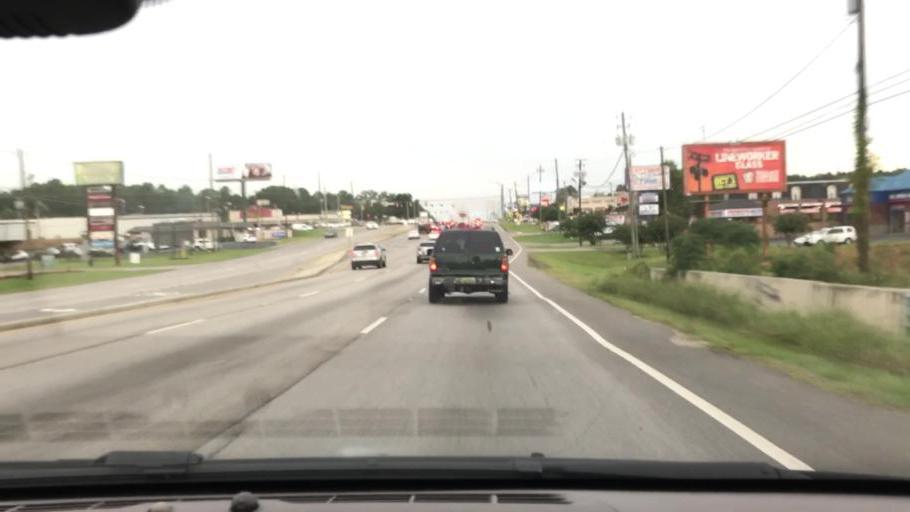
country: US
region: Alabama
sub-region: Houston County
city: Dothan
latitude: 31.2555
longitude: -85.4313
